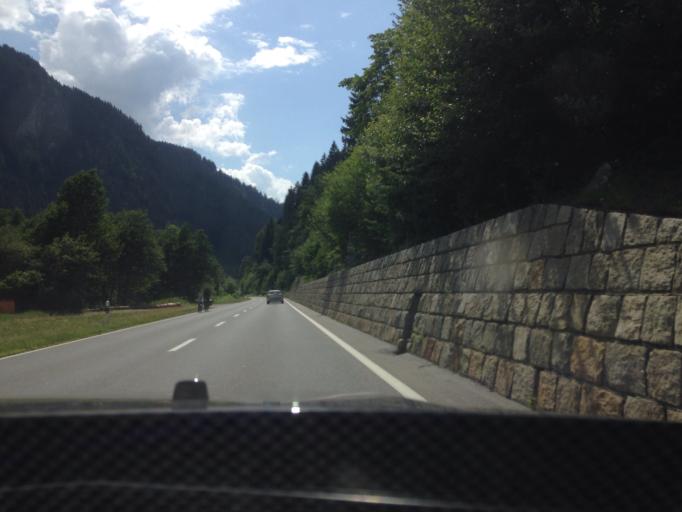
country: CH
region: Grisons
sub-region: Surselva District
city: Breil
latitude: 46.7607
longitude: 9.0922
